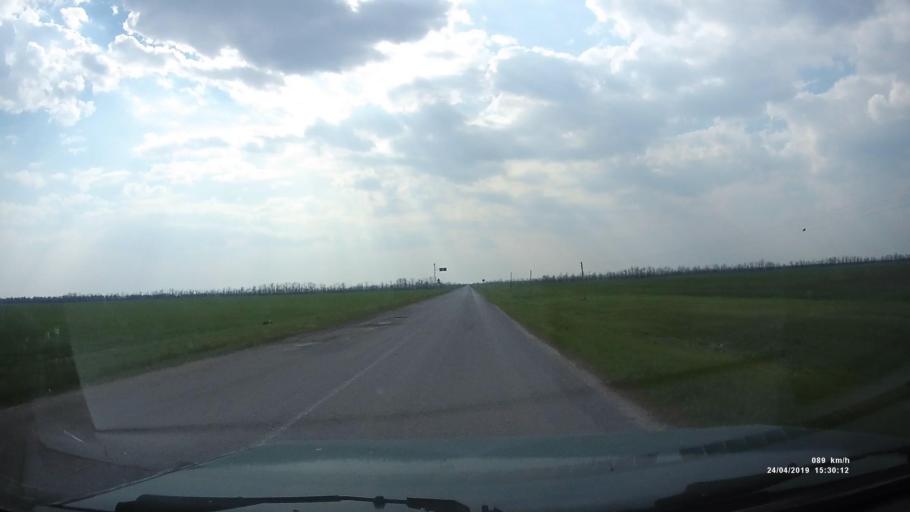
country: RU
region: Rostov
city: Remontnoye
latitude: 46.5998
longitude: 43.0116
